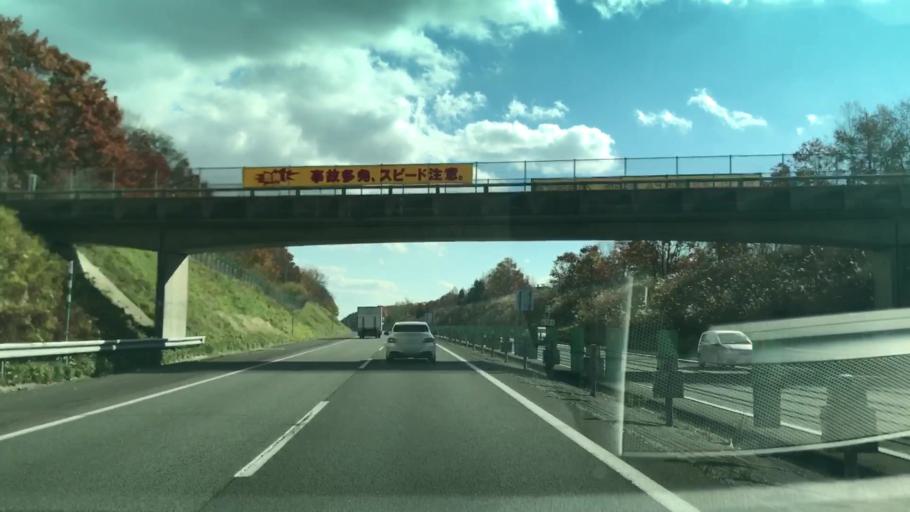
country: JP
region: Hokkaido
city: Kitahiroshima
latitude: 42.9373
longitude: 141.5243
